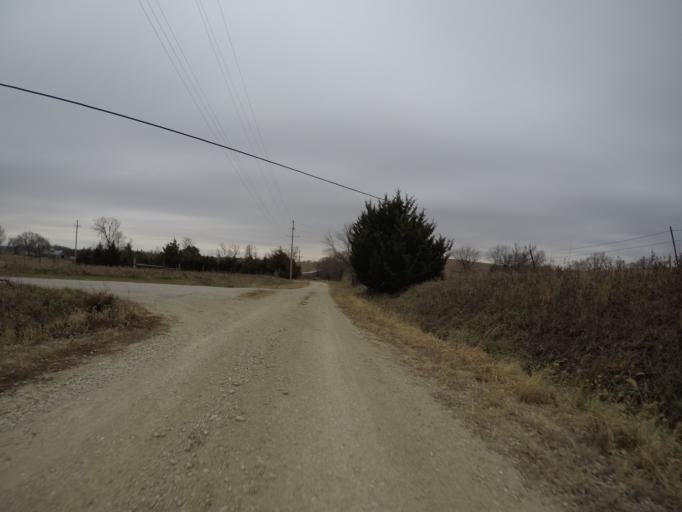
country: US
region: Kansas
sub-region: Wabaunsee County
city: Alma
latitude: 38.8561
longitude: -96.1133
